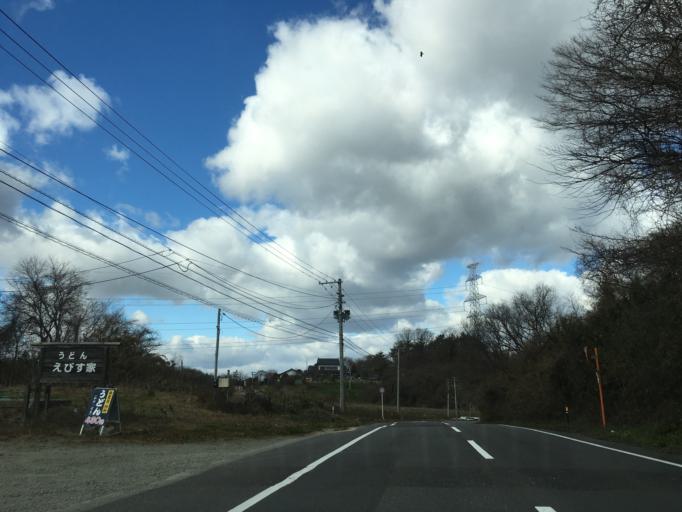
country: JP
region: Fukushima
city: Sukagawa
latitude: 37.3339
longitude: 140.4411
